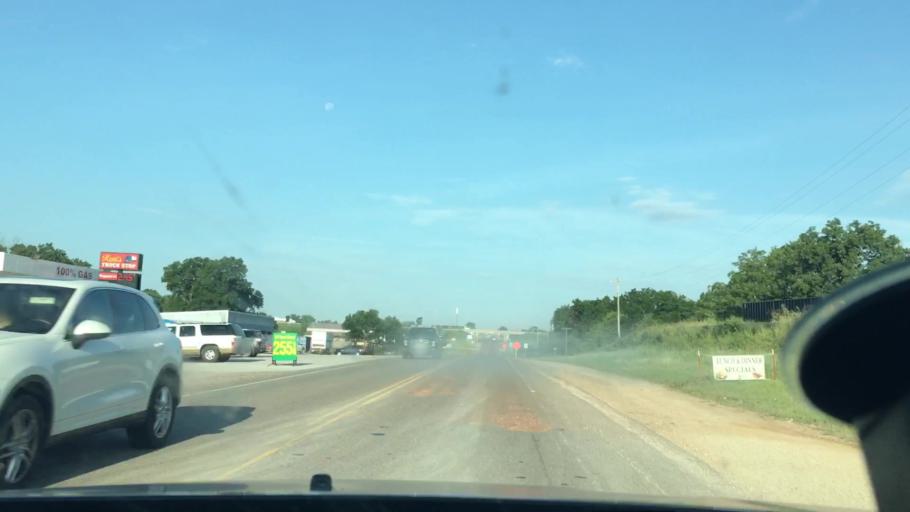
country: US
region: Oklahoma
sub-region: Garvin County
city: Wynnewood
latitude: 34.6517
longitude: -97.2143
